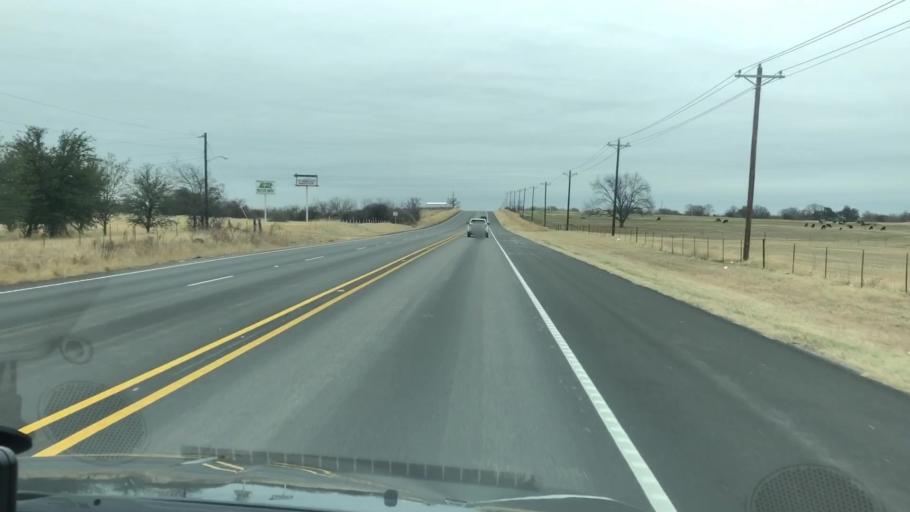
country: US
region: Texas
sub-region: Erath County
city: Stephenville
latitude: 32.2903
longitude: -98.1908
